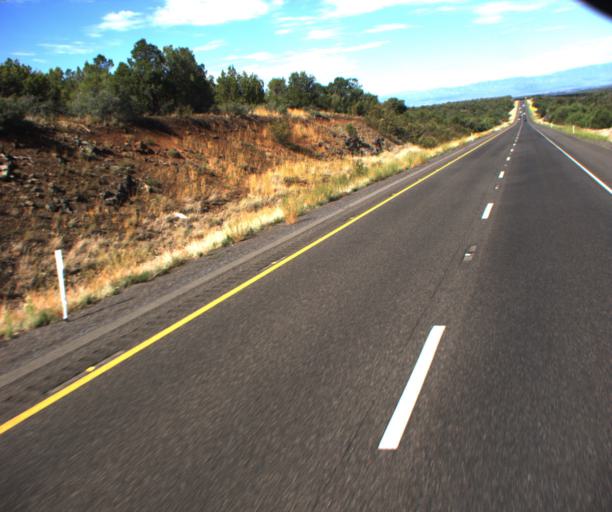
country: US
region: Arizona
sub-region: Yavapai County
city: Village of Oak Creek (Big Park)
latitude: 34.7814
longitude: -111.6180
